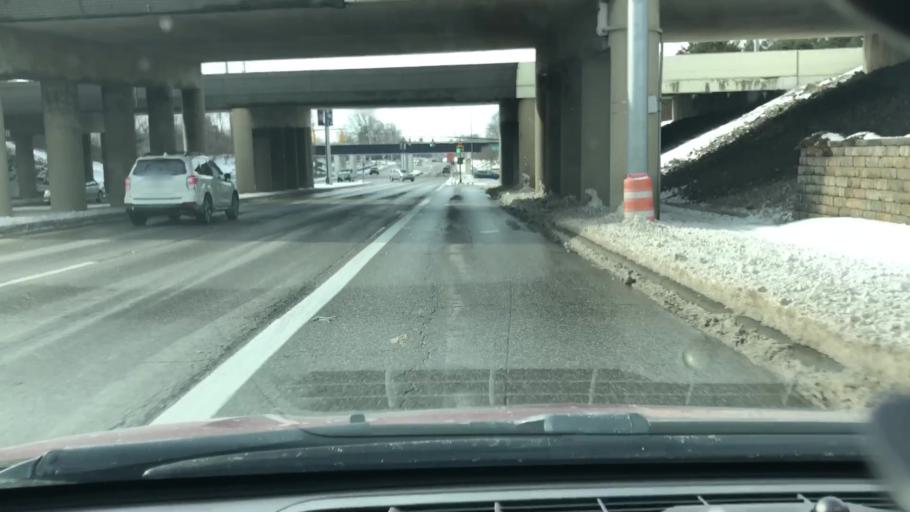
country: US
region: Ohio
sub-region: Franklin County
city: Worthington
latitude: 40.0617
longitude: -82.9975
